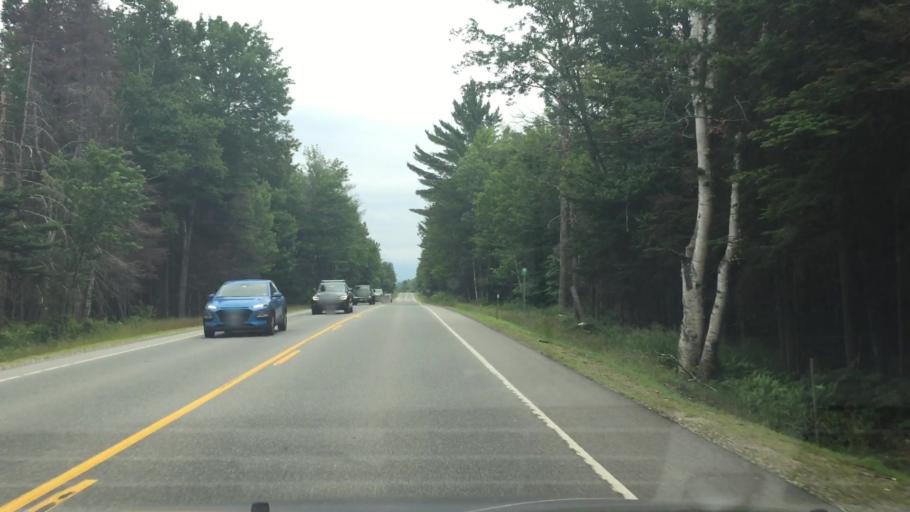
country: US
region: New Hampshire
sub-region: Grafton County
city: Deerfield
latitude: 44.2461
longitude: -71.6226
